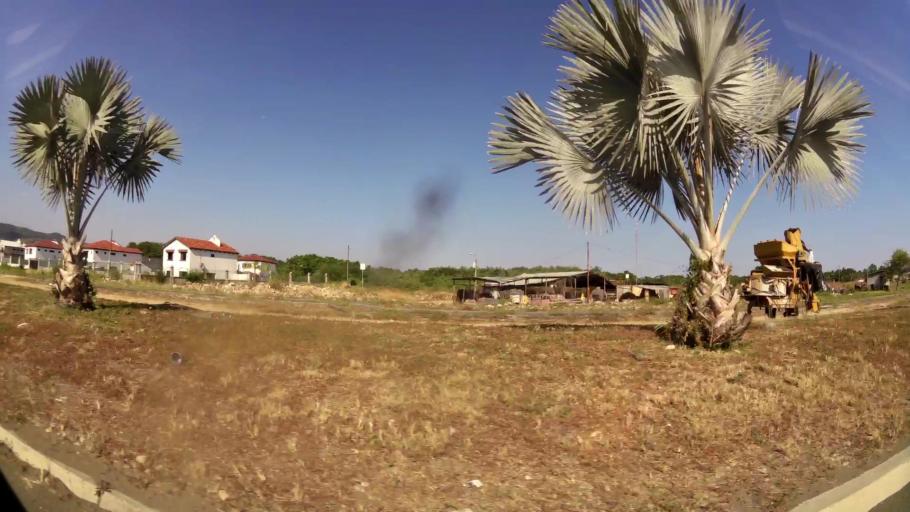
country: EC
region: Guayas
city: Santa Lucia
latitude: -2.1880
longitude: -80.0010
